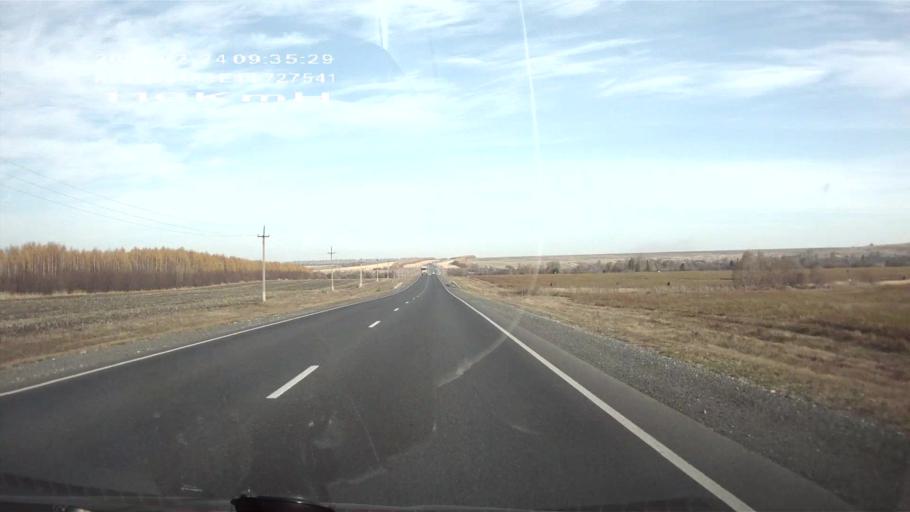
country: RU
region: Penza
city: Mokshan
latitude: 53.6046
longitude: 44.7276
